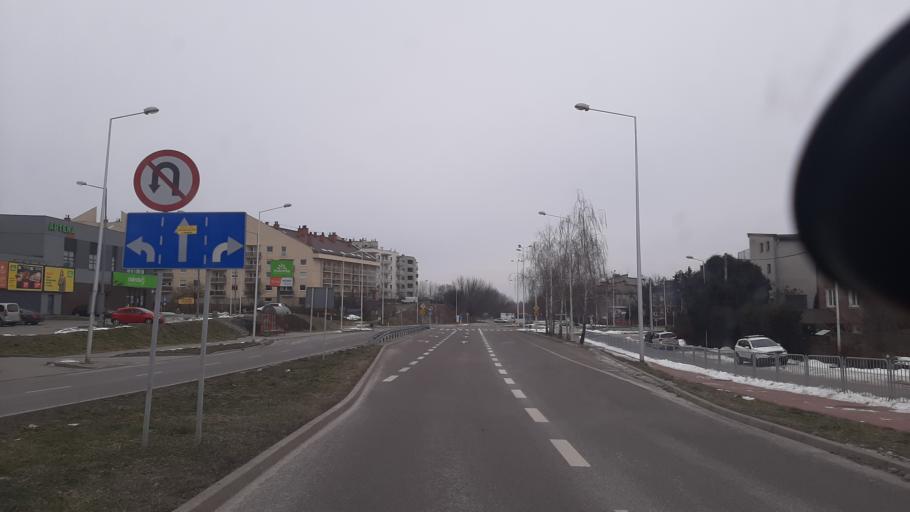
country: PL
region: Lublin Voivodeship
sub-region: Powiat lubelski
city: Lublin
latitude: 51.2700
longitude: 22.5806
